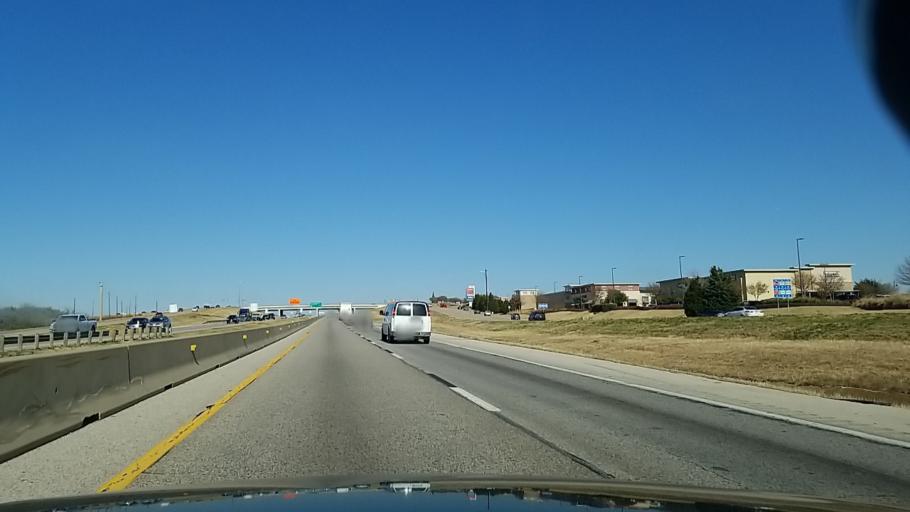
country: US
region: Texas
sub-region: Tarrant County
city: Blue Mound
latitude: 32.9095
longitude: -97.3171
